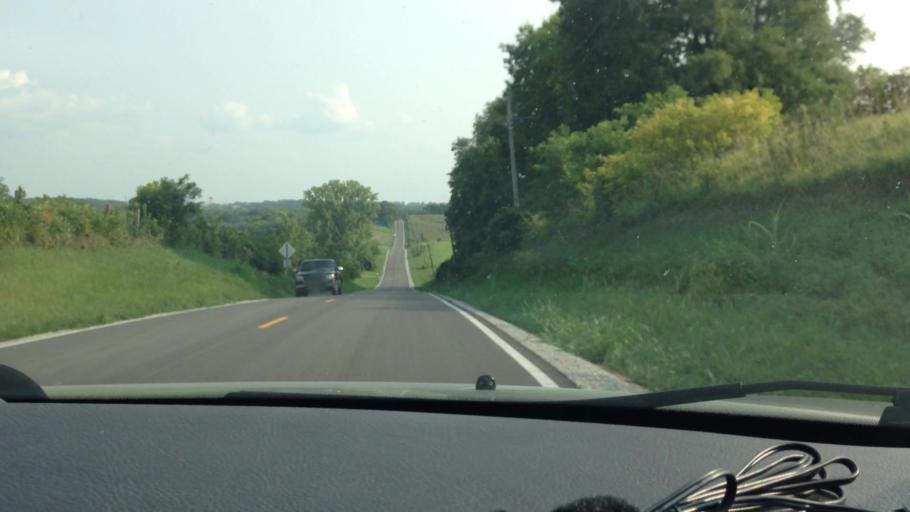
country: US
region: Missouri
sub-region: Platte County
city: Platte City
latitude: 39.3989
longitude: -94.7797
